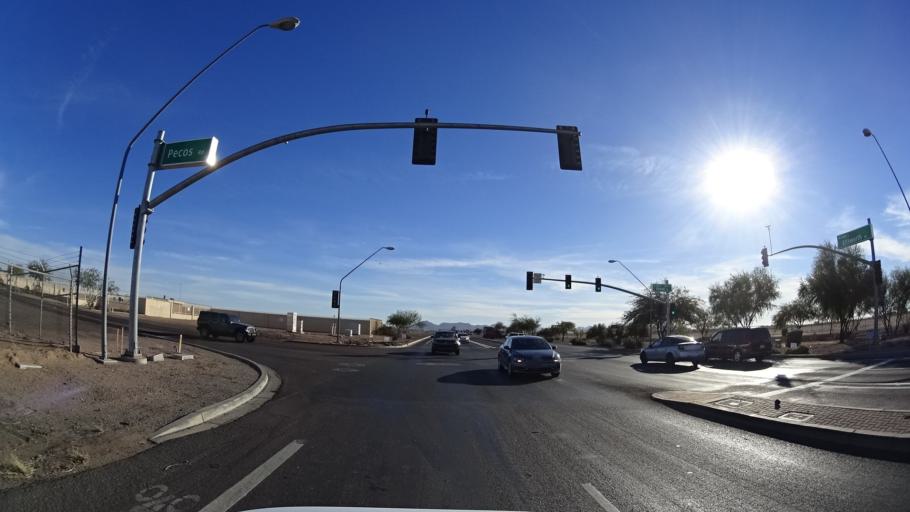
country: US
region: Arizona
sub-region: Maricopa County
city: Queen Creek
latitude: 33.2924
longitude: -111.6349
